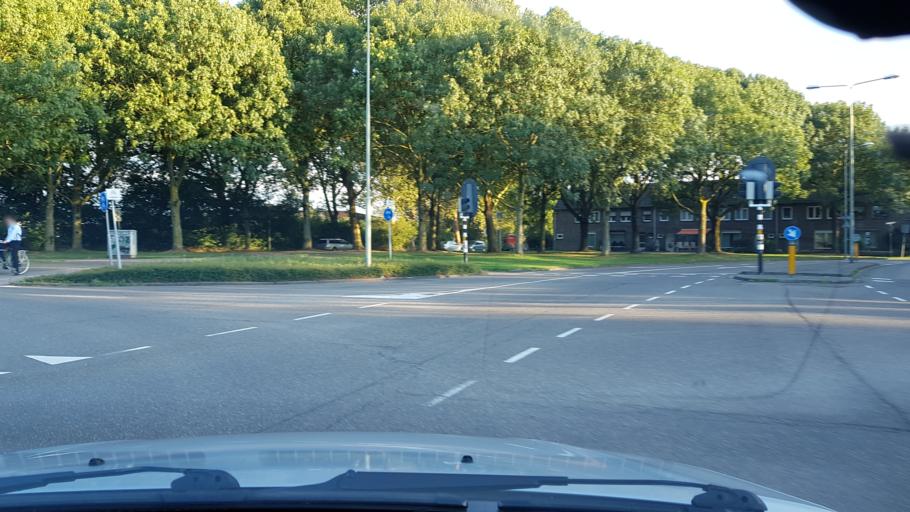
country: NL
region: Limburg
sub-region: Gemeente Sittard-Geleen
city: Limbricht
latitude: 50.9841
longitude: 5.8259
